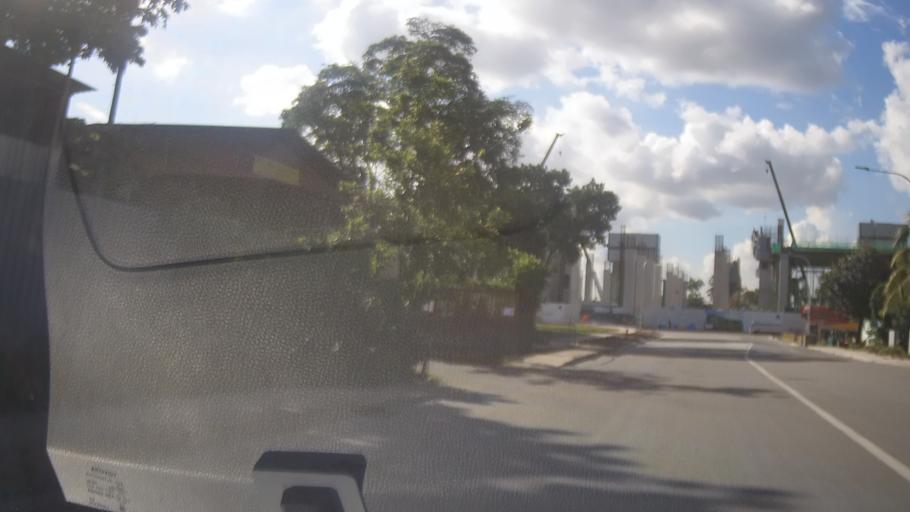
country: MY
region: Johor
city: Johor Bahru
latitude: 1.4357
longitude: 103.7582
